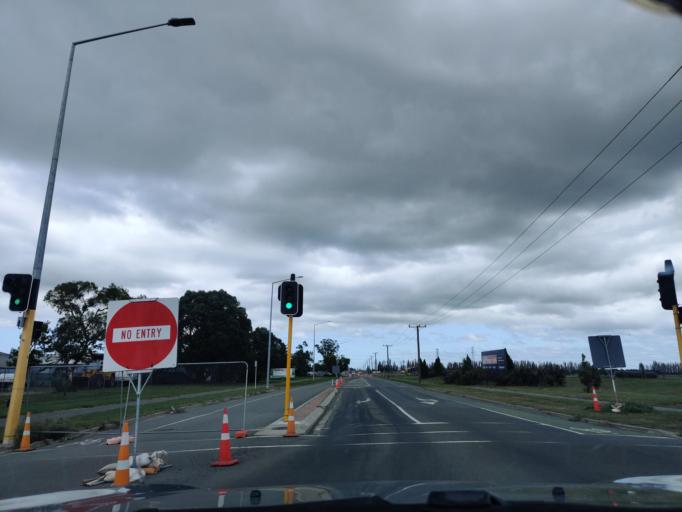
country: NZ
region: Canterbury
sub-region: Selwyn District
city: Prebbleton
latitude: -43.5556
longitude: 172.5121
